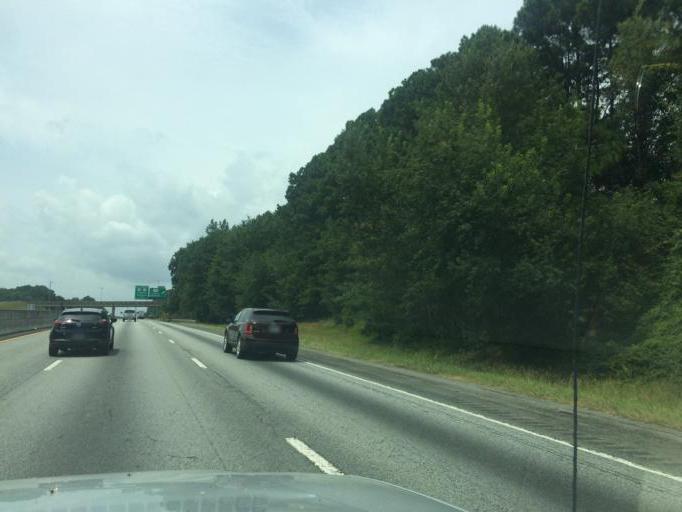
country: US
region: South Carolina
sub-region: Anderson County
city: Northlake
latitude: 34.5809
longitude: -82.6888
